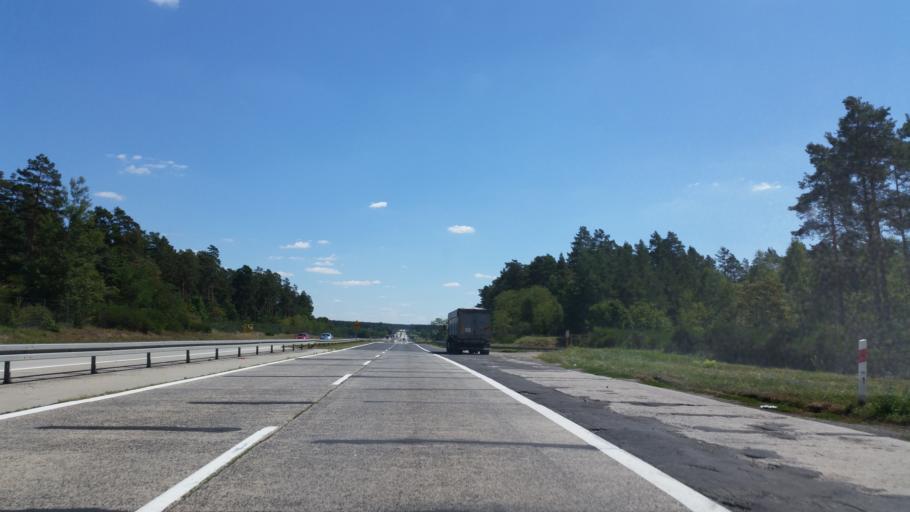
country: PL
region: Lower Silesian Voivodeship
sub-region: Powiat boleslawiecki
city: Boleslawiec
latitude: 51.3662
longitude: 15.5731
